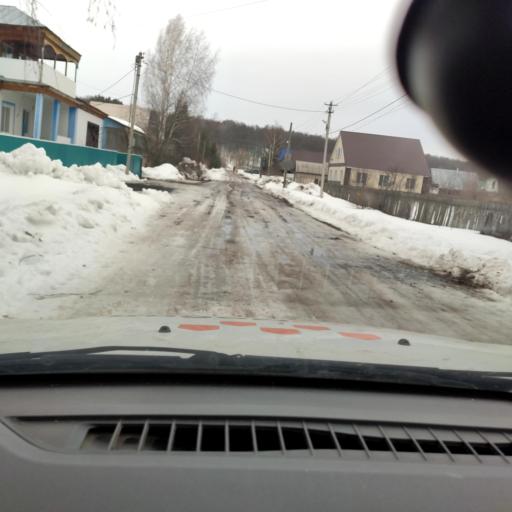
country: RU
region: Bashkortostan
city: Ufa
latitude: 54.5254
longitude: 55.9163
